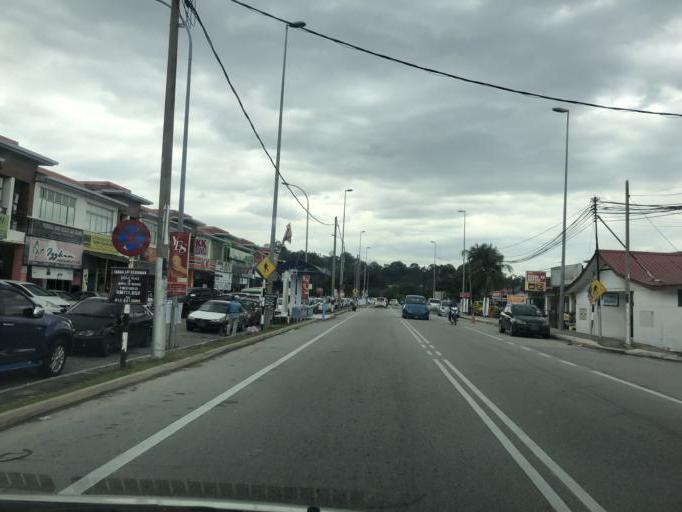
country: MY
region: Putrajaya
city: Putrajaya
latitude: 2.9247
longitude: 101.7593
